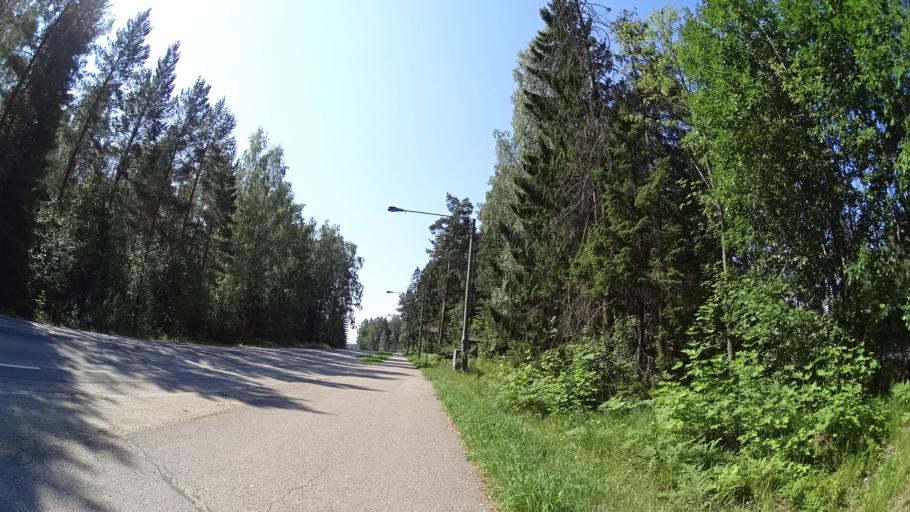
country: FI
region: Uusimaa
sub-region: Helsinki
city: Kerava
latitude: 60.3717
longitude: 25.0767
